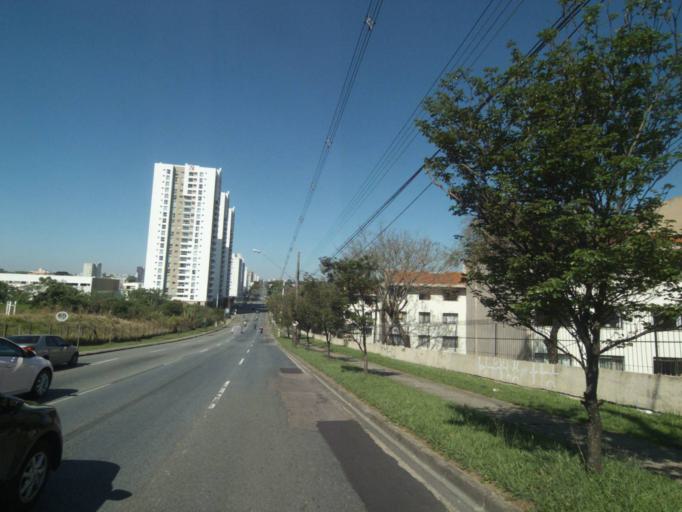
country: BR
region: Parana
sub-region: Curitiba
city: Curitiba
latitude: -25.3860
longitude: -49.2350
